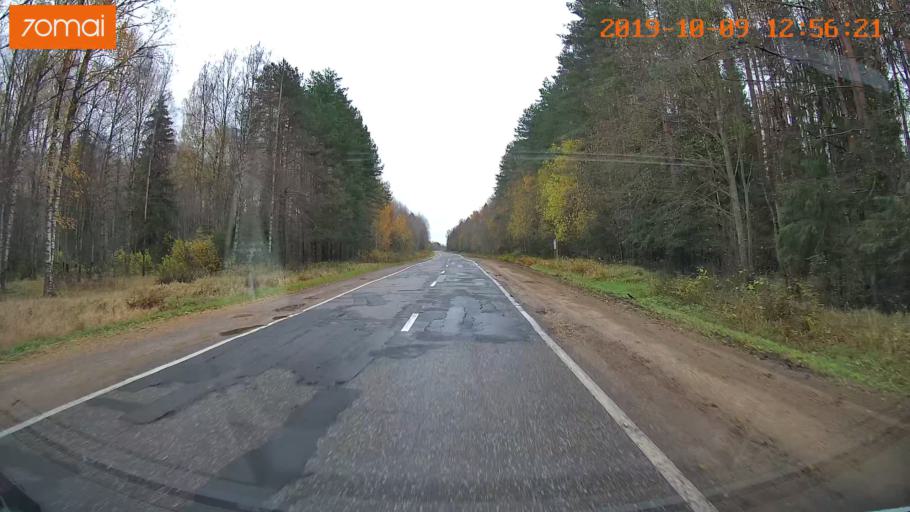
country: RU
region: Jaroslavl
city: Prechistoye
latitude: 58.3950
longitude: 40.4145
